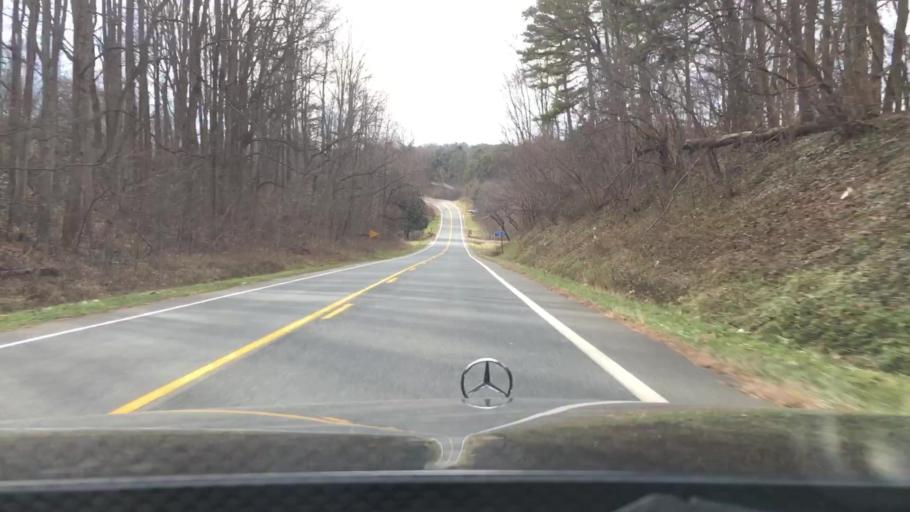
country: US
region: Virginia
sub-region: Pittsylvania County
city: Hurt
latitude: 37.0891
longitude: -79.3188
